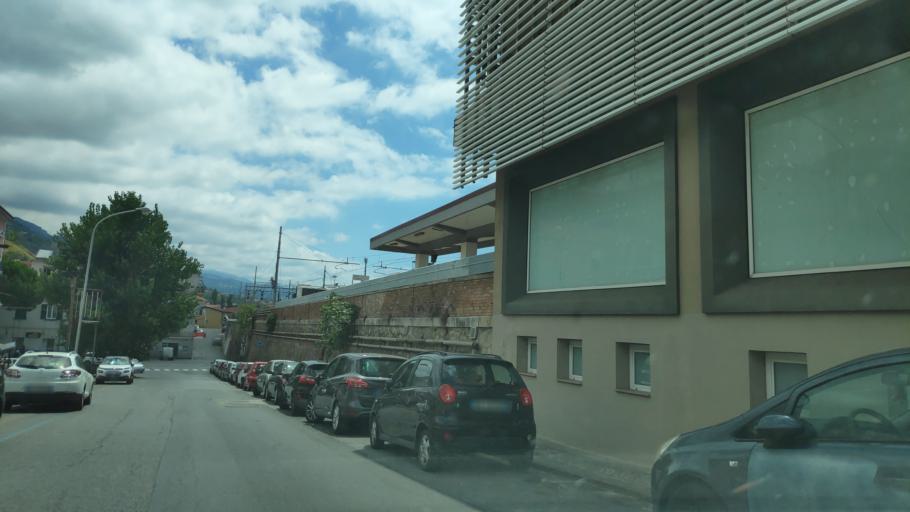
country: IT
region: Calabria
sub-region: Provincia di Cosenza
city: Paola
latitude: 39.3591
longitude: 16.0338
